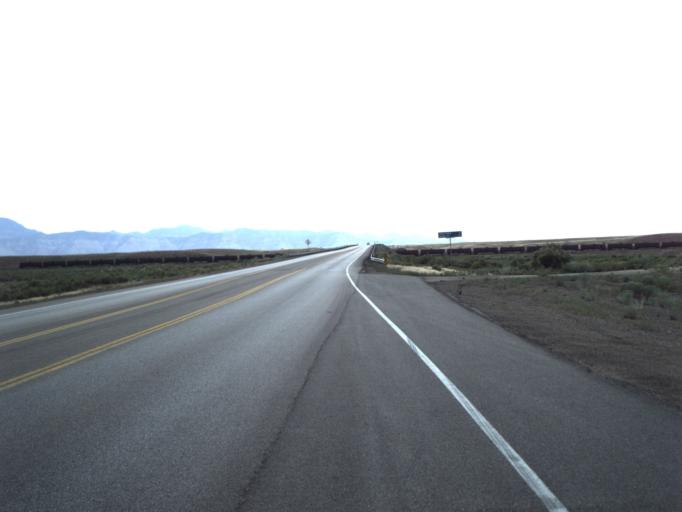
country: US
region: Utah
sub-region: Carbon County
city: East Carbon City
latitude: 39.5246
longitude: -110.5708
